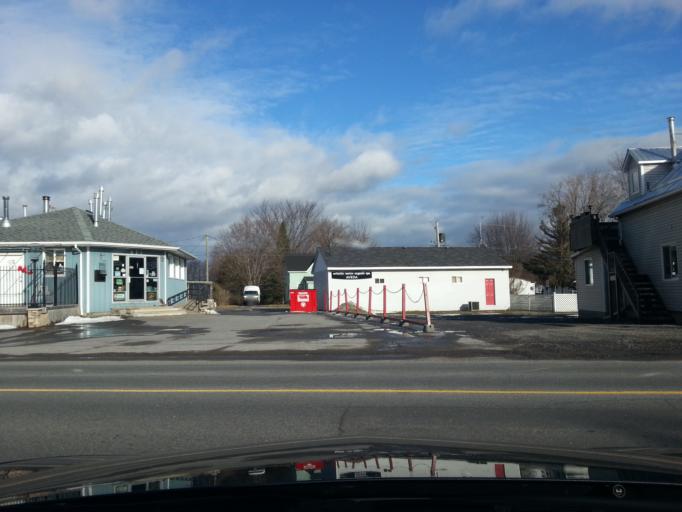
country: CA
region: Ontario
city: Prescott
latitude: 45.0190
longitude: -75.6506
